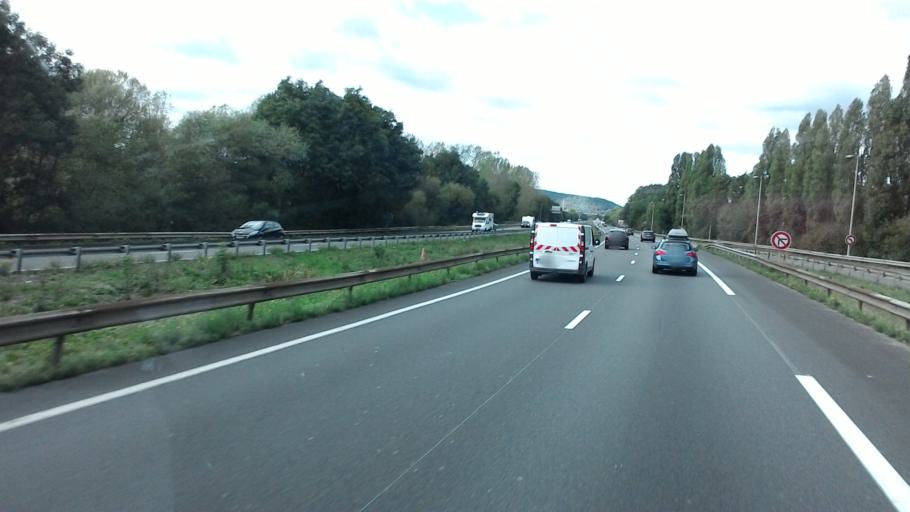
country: FR
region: Lorraine
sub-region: Departement de Meurthe-et-Moselle
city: Bouxieres-aux-Dames
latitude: 48.7542
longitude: 6.1560
